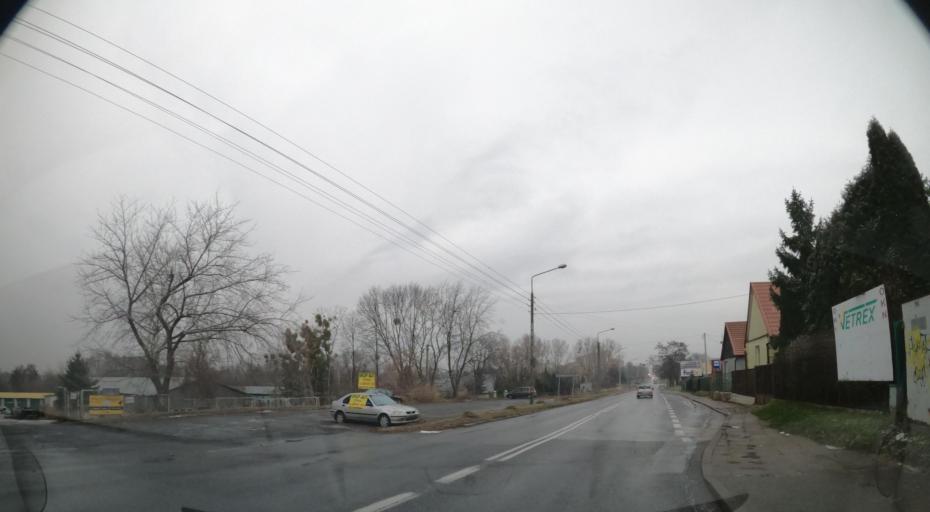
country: PL
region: Masovian Voivodeship
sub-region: Powiat radomski
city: Trablice
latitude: 51.3818
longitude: 21.1202
